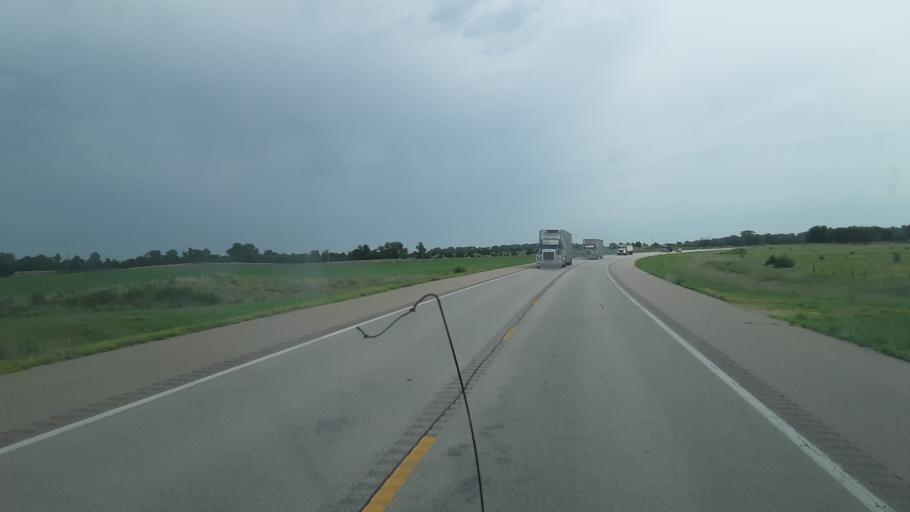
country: US
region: Kansas
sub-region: Stafford County
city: Stafford
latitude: 37.9813
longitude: -98.3910
